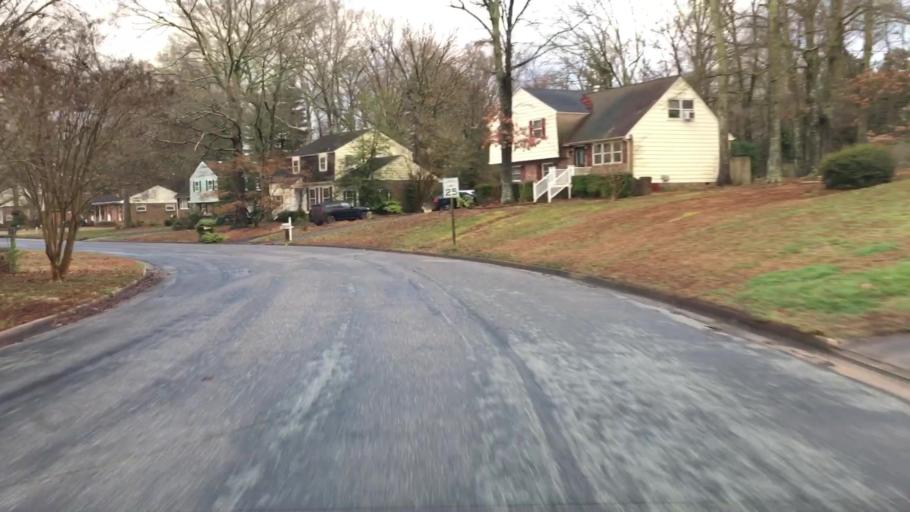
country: US
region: Virginia
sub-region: Chesterfield County
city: Bon Air
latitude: 37.5147
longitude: -77.6244
